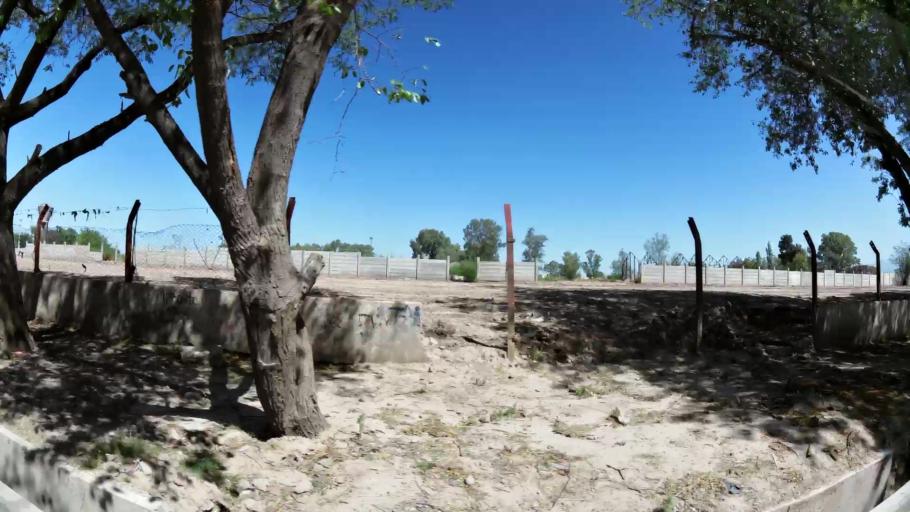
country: AR
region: Mendoza
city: Mendoza
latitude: -32.8854
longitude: -68.8100
